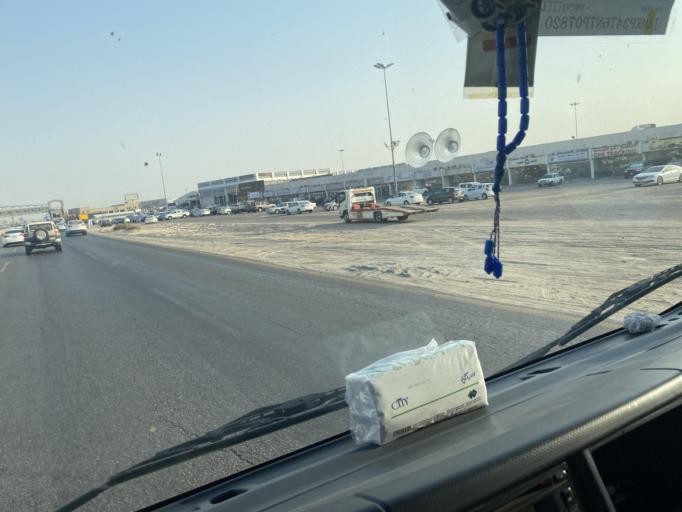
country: SA
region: Eastern Province
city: Sayhat
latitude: 26.4062
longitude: 50.0148
